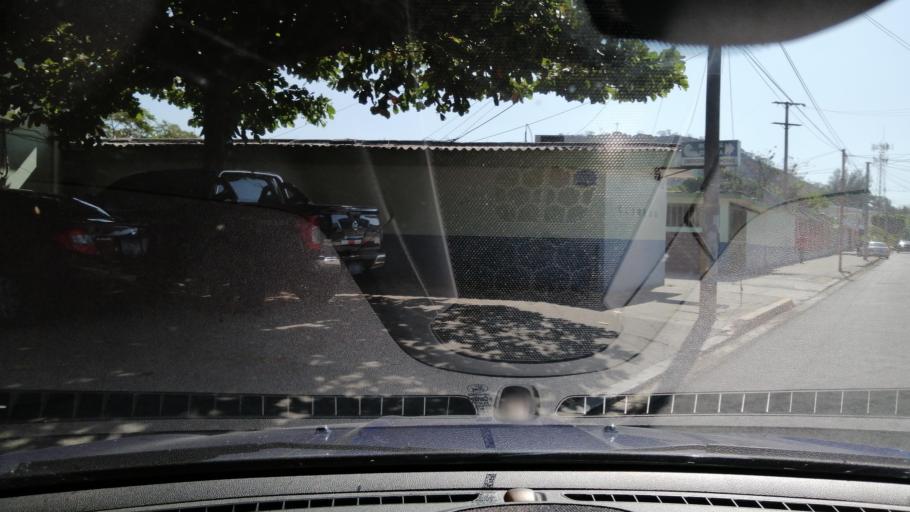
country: SV
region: Santa Ana
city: Santa Ana
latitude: 13.9935
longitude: -89.5483
